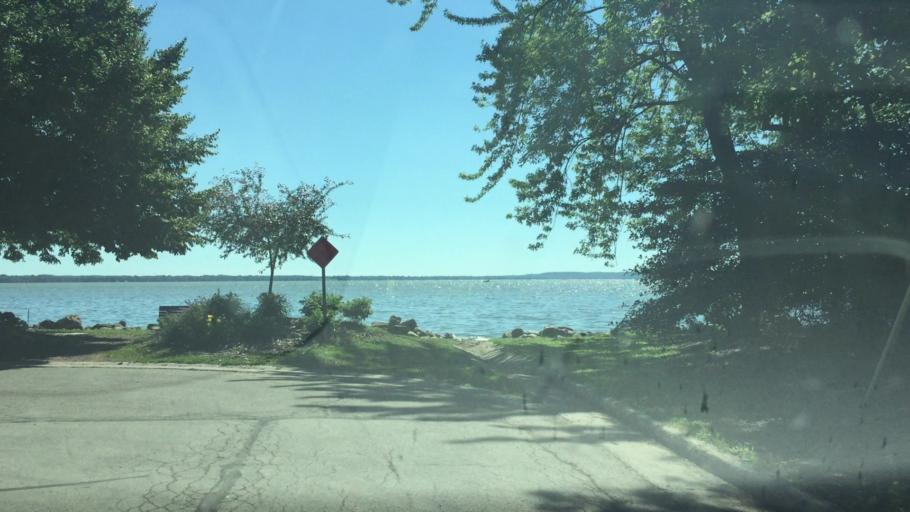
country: US
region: Wisconsin
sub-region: Winnebago County
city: Menasha
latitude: 44.1935
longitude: -88.4345
